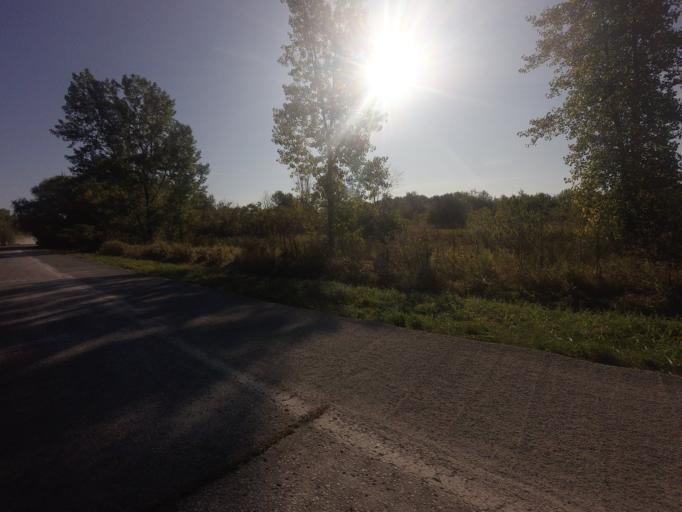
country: CA
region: Quebec
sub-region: Laurentides
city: Oka
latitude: 45.4760
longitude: -74.0570
